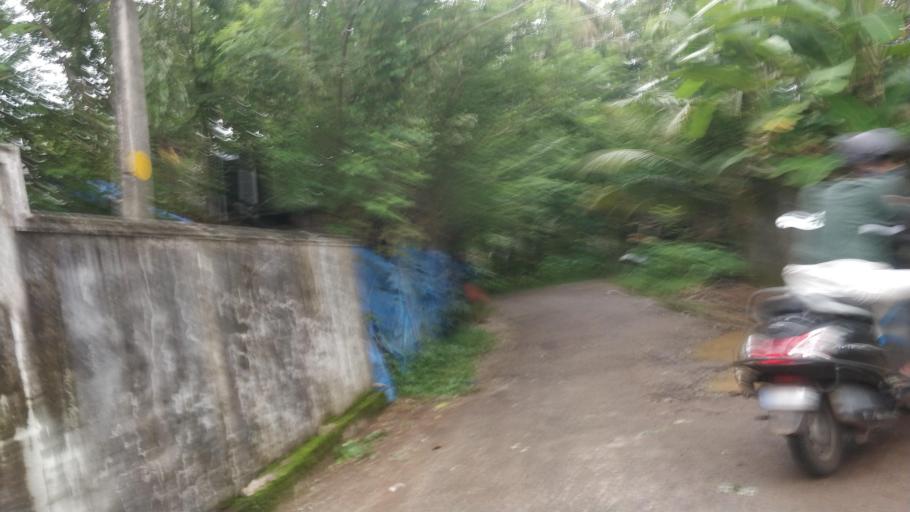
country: IN
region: Kerala
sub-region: Alappuzha
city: Shertallai
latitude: 9.6974
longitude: 76.3598
